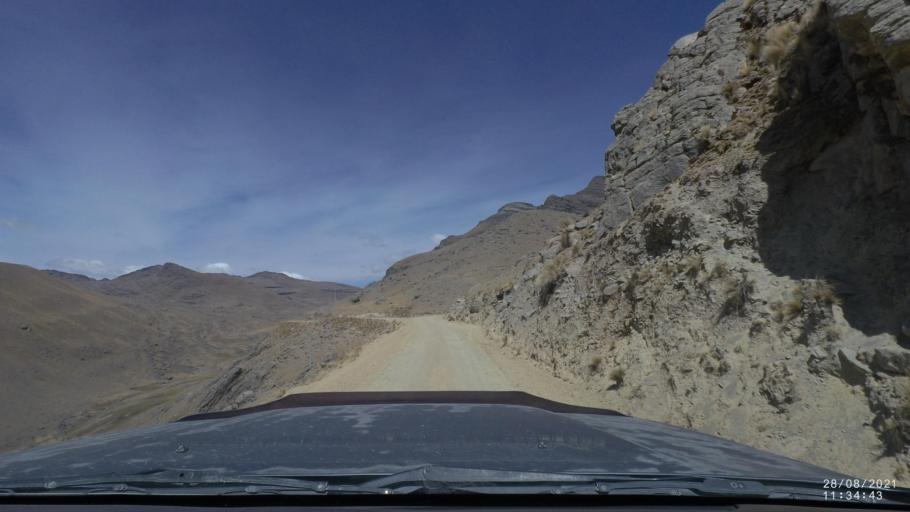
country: BO
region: Cochabamba
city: Sipe Sipe
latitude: -17.1925
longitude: -66.3747
